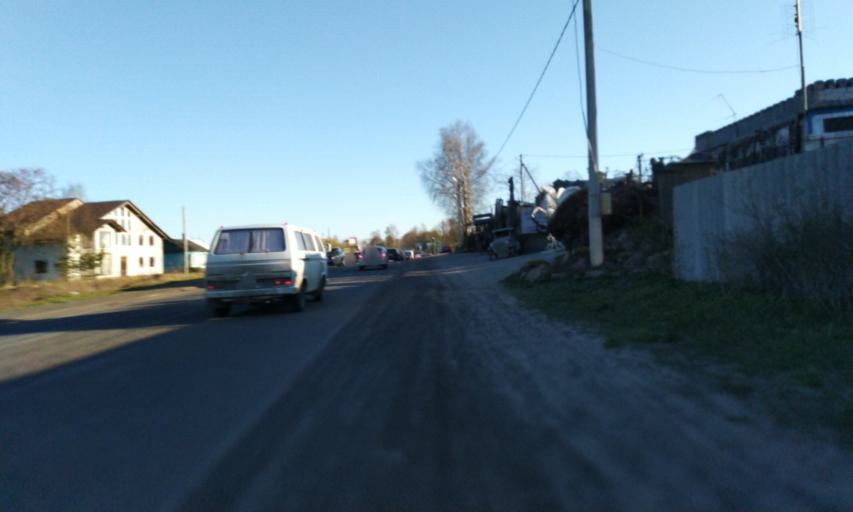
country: RU
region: Leningrad
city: Toksovo
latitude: 60.1152
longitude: 30.5032
